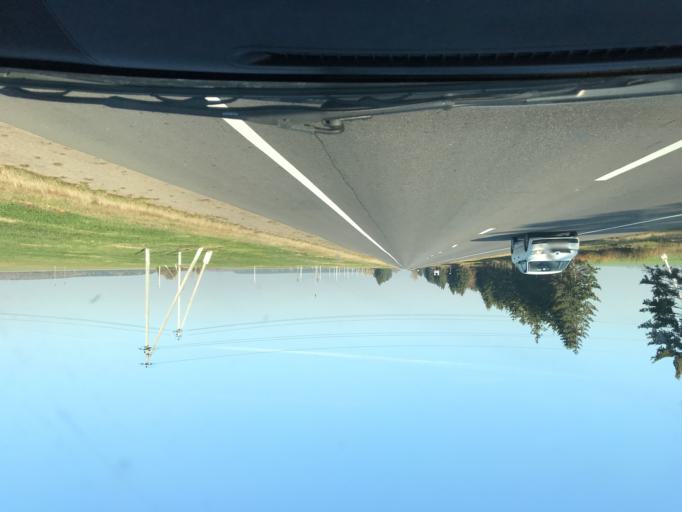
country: BY
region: Mogilev
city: Shklow
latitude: 54.2598
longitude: 30.4503
